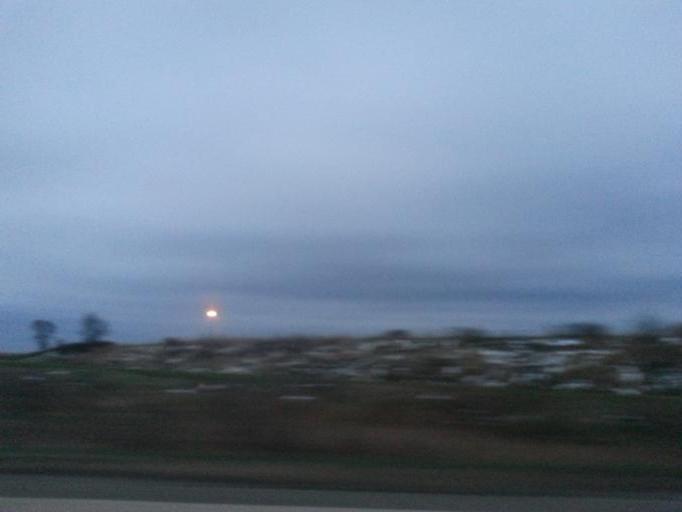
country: US
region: Iowa
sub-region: Black Hawk County
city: Elk Run Heights
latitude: 42.4471
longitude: -92.1895
